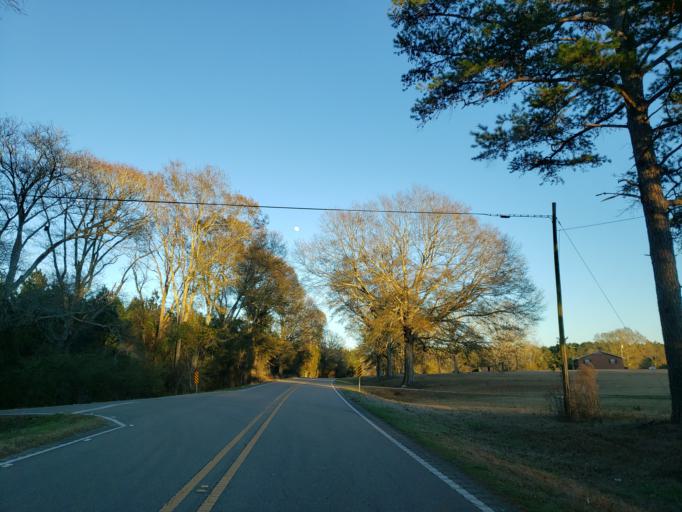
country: US
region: Mississippi
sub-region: Covington County
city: Collins
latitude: 31.5651
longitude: -89.4367
